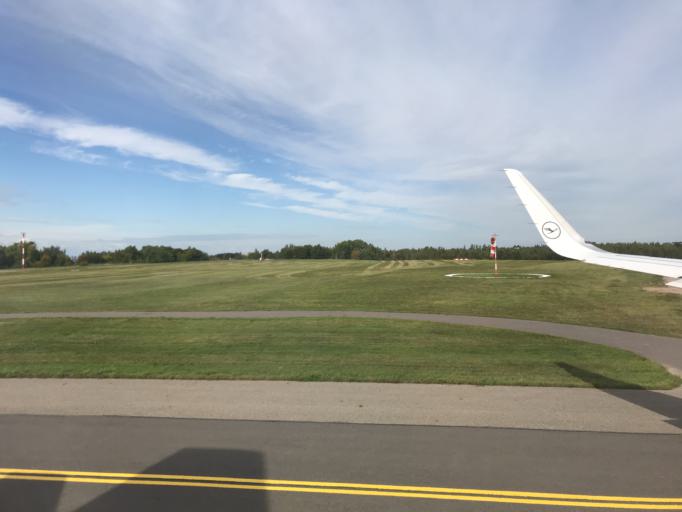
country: LT
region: Vilnius County
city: Naujamiestis
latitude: 54.6431
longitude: 25.2891
